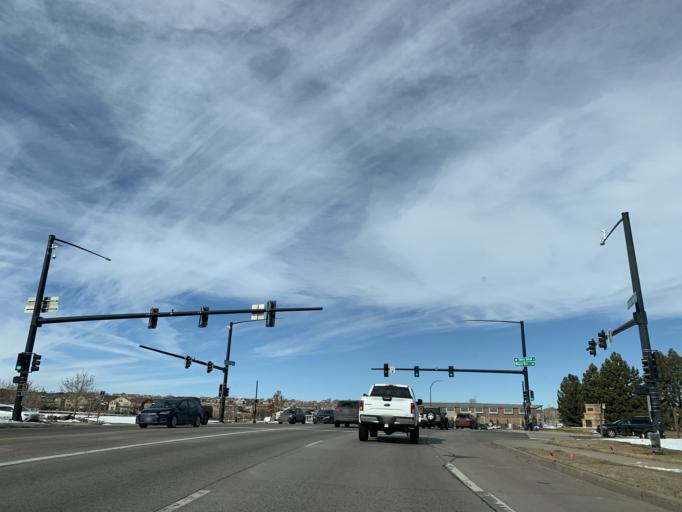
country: US
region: Colorado
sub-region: Douglas County
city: Carriage Club
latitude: 39.5218
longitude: -104.9304
